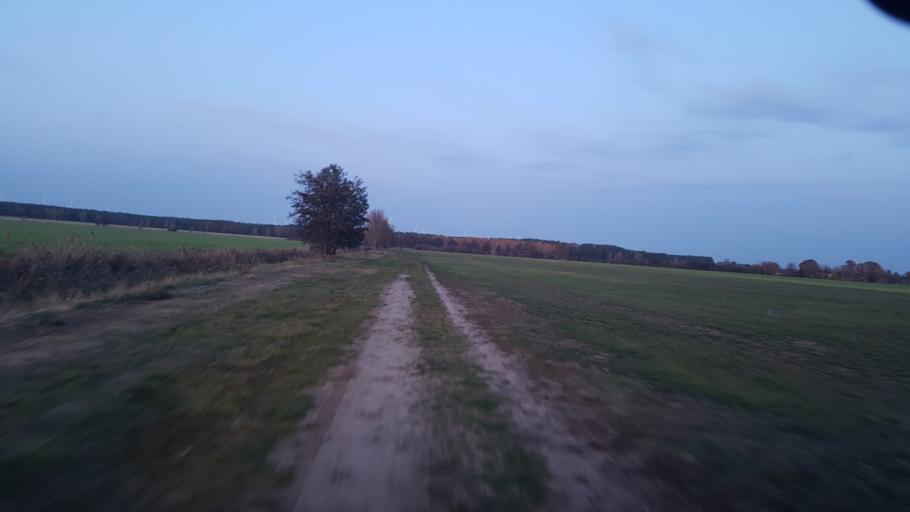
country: DE
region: Brandenburg
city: Schilda
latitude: 51.6301
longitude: 13.3348
